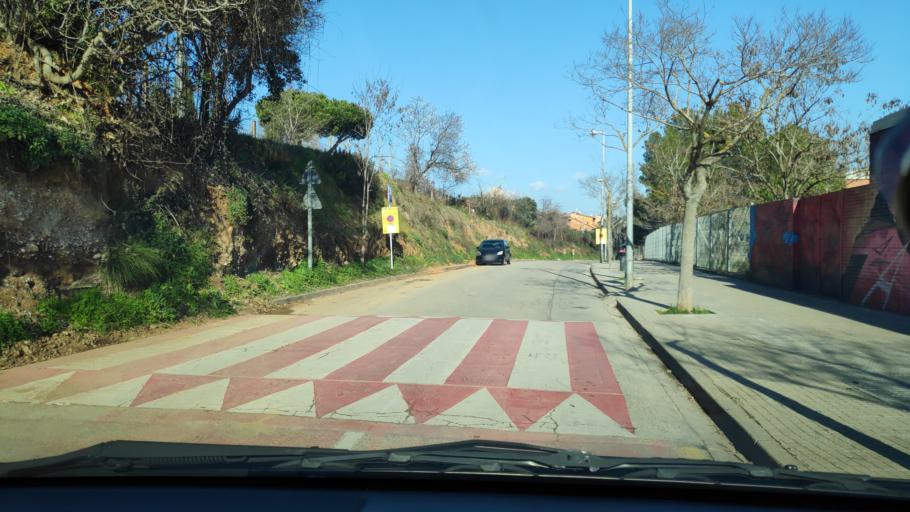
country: ES
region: Catalonia
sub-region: Provincia de Barcelona
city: Sant Cugat del Valles
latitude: 41.4595
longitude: 2.0692
